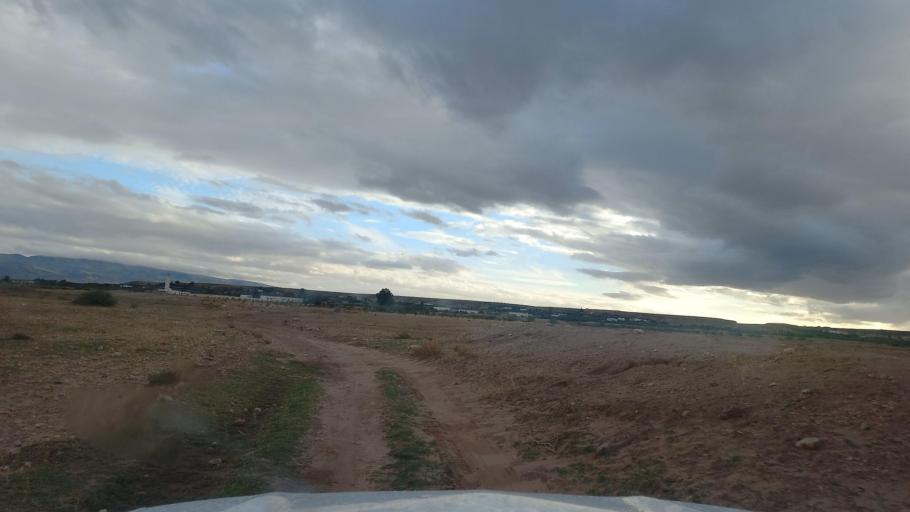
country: TN
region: Al Qasrayn
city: Kasserine
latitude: 35.2709
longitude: 8.9364
